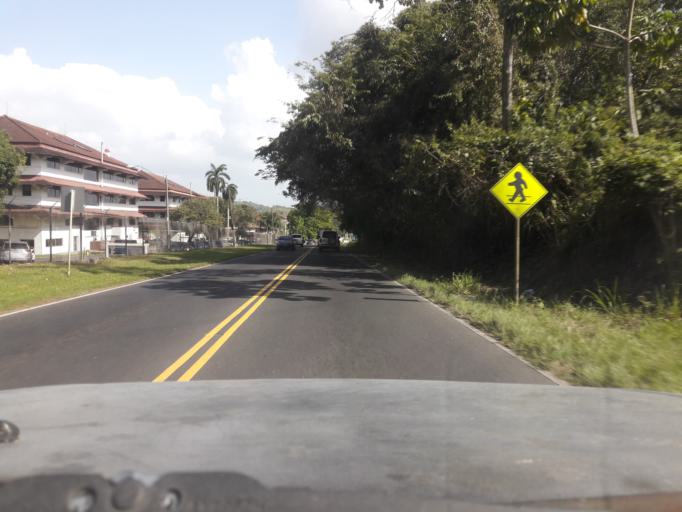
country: PA
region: Panama
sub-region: Distrito de Panama
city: Paraiso
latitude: 9.0045
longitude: -79.5907
